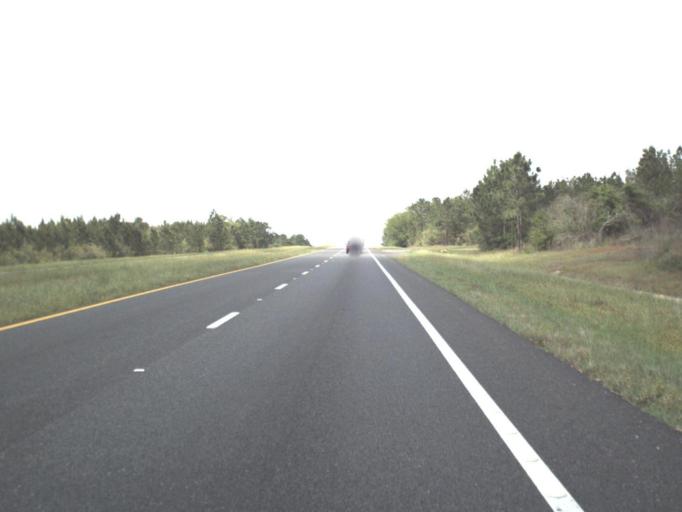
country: US
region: Florida
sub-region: Escambia County
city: Molino
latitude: 30.8066
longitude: -87.3359
